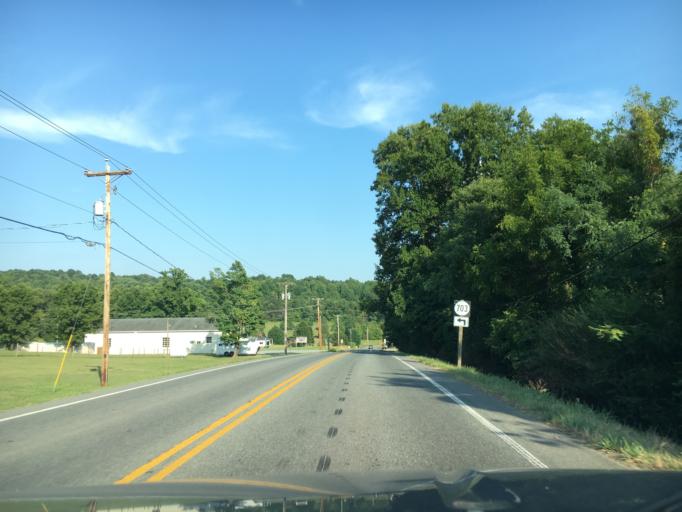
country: US
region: Virginia
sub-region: Franklin County
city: Union Hall
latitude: 37.0047
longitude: -79.7741
